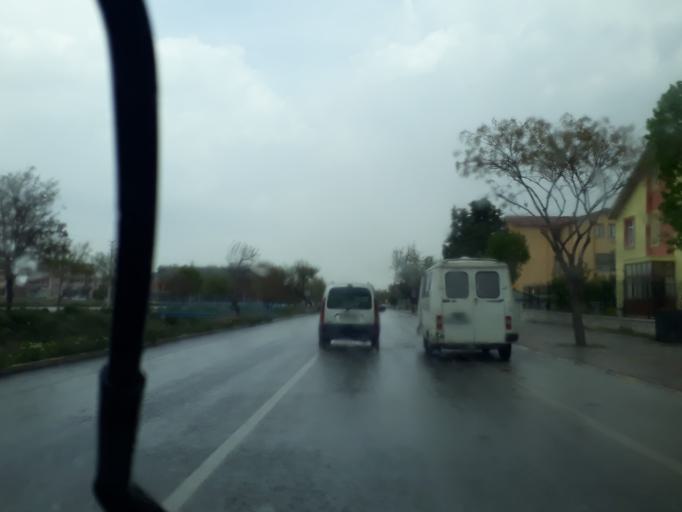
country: TR
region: Konya
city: Selcuklu
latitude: 37.9190
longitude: 32.4839
